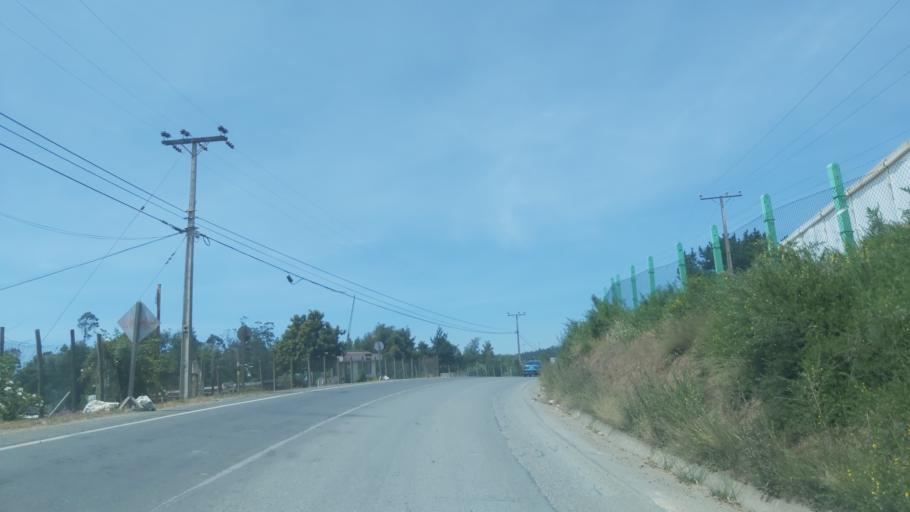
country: CL
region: Maule
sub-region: Provincia de Talca
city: Constitucion
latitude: -35.3751
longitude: -72.4195
